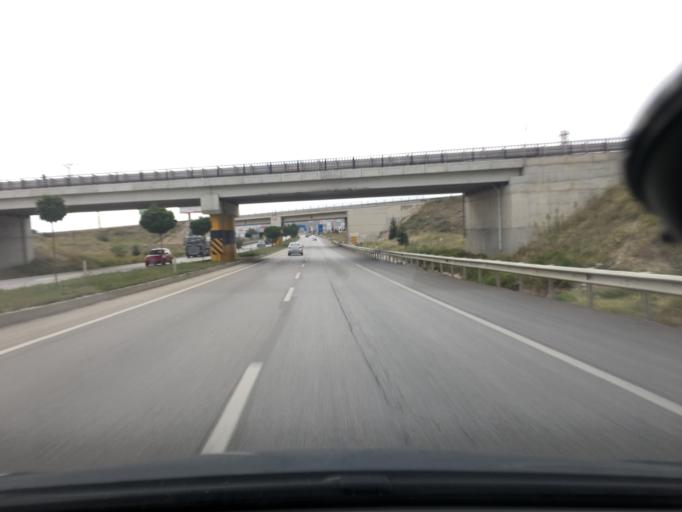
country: TR
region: Afyonkarahisar
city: Afyonkarahisar
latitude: 38.7944
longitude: 30.4018
